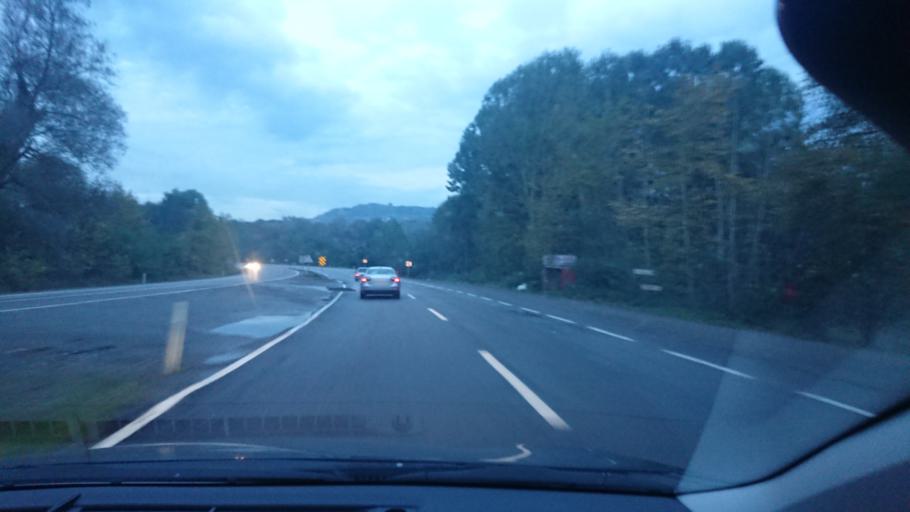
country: TR
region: Zonguldak
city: Beycuma
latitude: 41.3237
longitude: 32.0515
